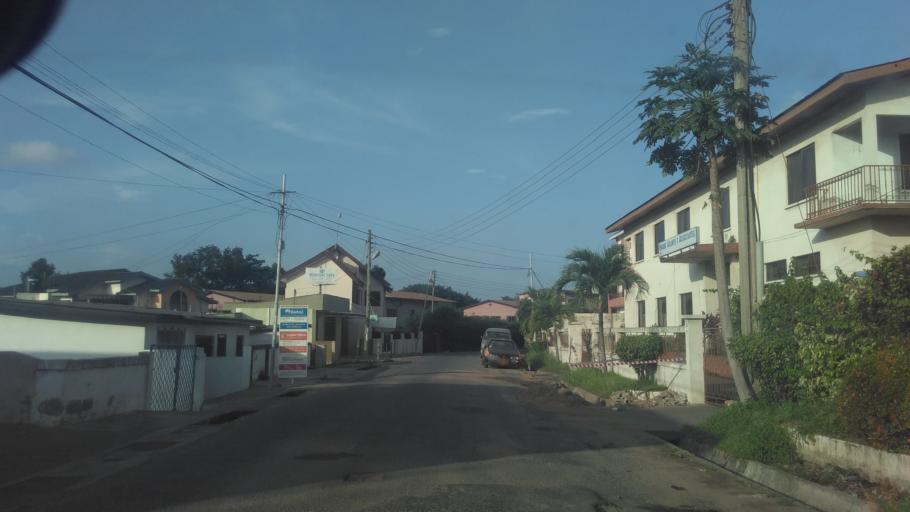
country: GH
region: Greater Accra
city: Accra
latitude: 5.5708
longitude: -0.2052
